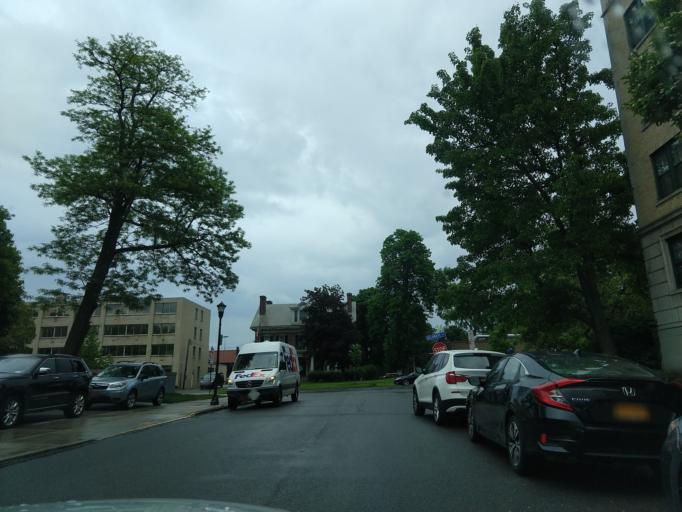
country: US
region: New York
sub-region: Erie County
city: Buffalo
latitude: 42.9181
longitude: -78.8691
